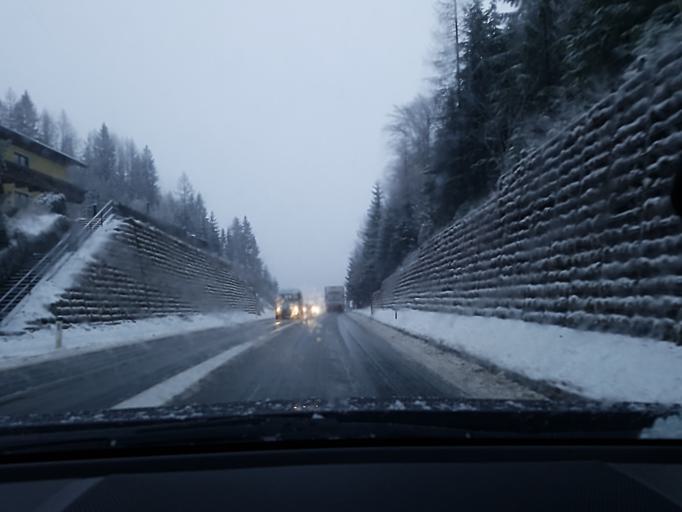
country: AT
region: Salzburg
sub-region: Politischer Bezirk Hallein
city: Scheffau am Tennengebirge
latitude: 47.5837
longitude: 13.2700
